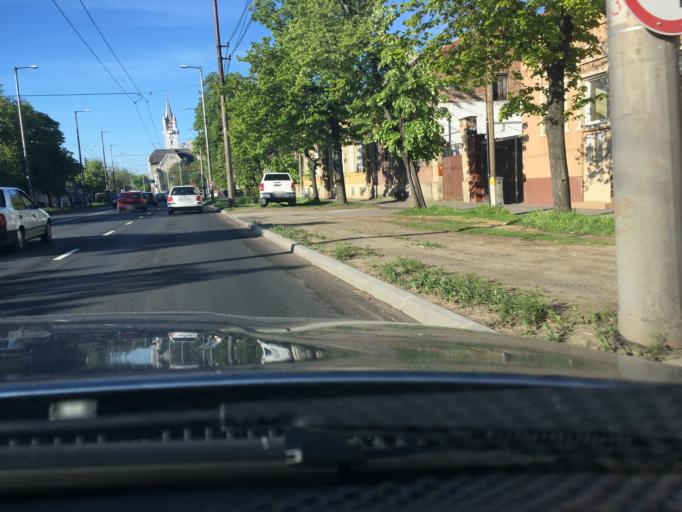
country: HU
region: Hajdu-Bihar
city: Debrecen
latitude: 47.5403
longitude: 21.6399
